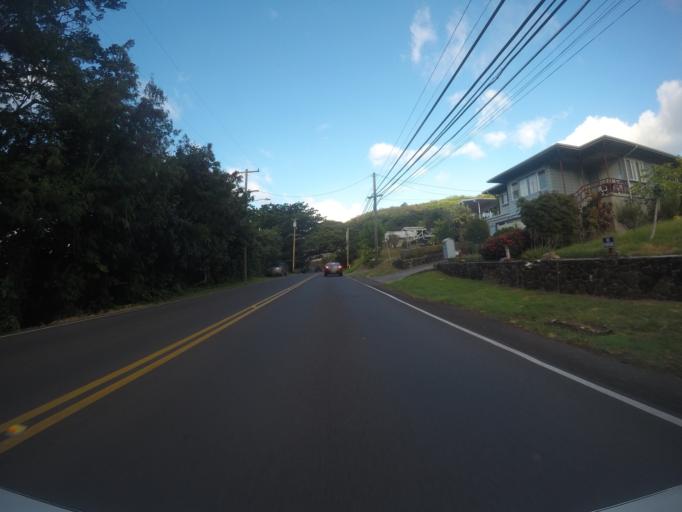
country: US
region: Hawaii
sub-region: Honolulu County
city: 'Ahuimanu
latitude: 21.4523
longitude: -157.8205
